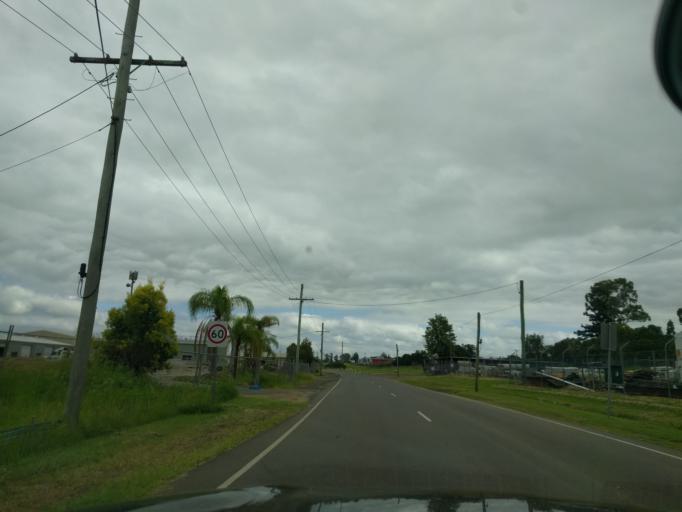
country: AU
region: Queensland
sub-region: Logan
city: Cedar Vale
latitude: -27.9862
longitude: 152.9944
